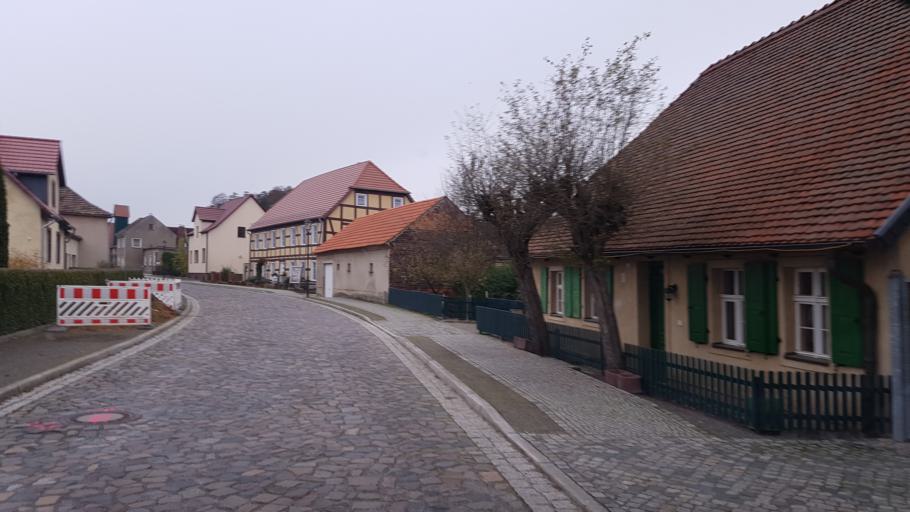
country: DE
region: Brandenburg
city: Crinitz
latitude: 51.7589
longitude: 13.8056
